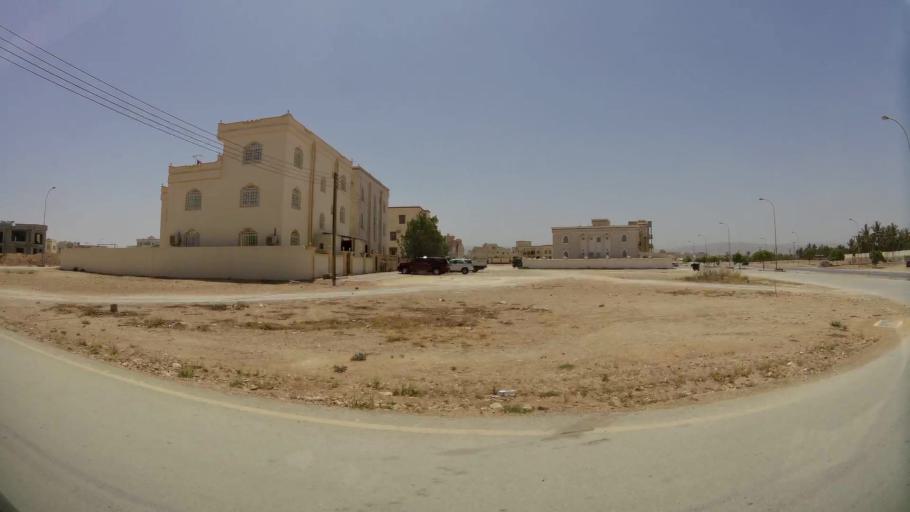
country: OM
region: Zufar
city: Salalah
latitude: 17.0606
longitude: 54.1618
